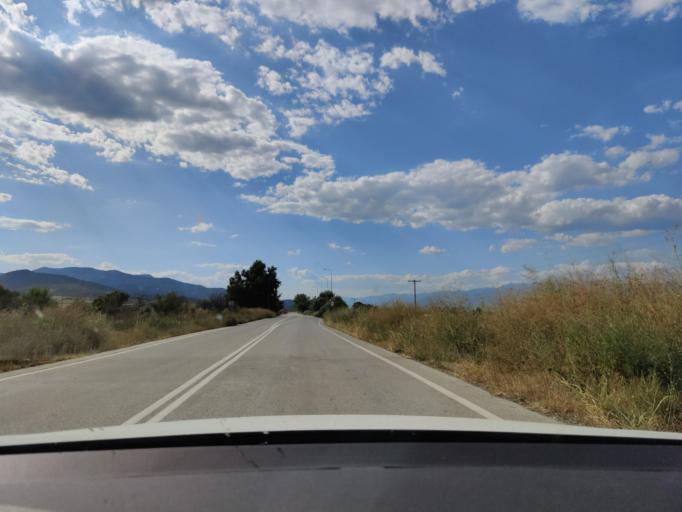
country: GR
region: Central Macedonia
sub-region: Nomos Serron
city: Strymoniko
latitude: 41.0897
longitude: 23.2815
